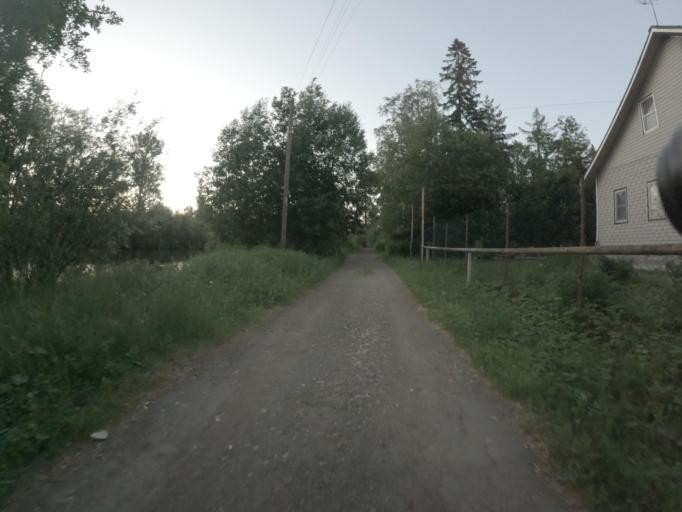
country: RU
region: Leningrad
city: Vsevolozhsk
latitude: 60.0138
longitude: 30.6112
